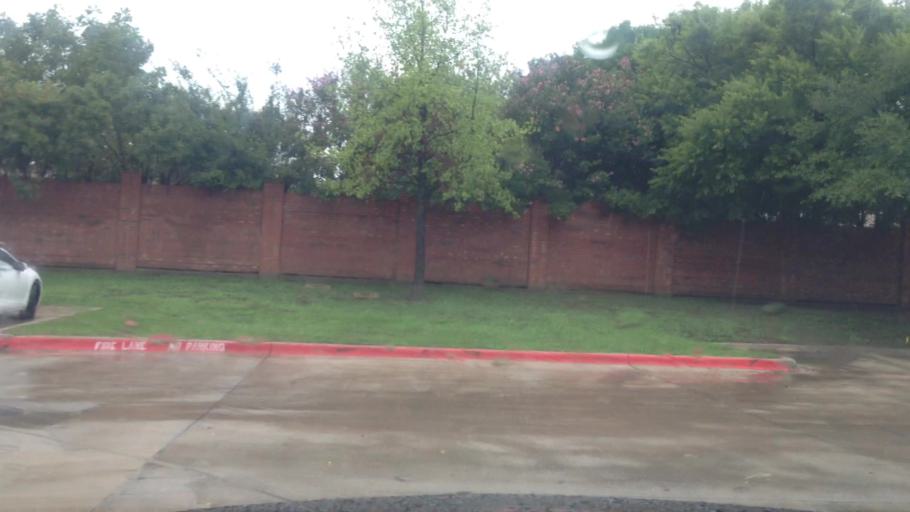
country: US
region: Texas
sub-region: Tarrant County
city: Watauga
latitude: 32.8777
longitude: -97.2353
